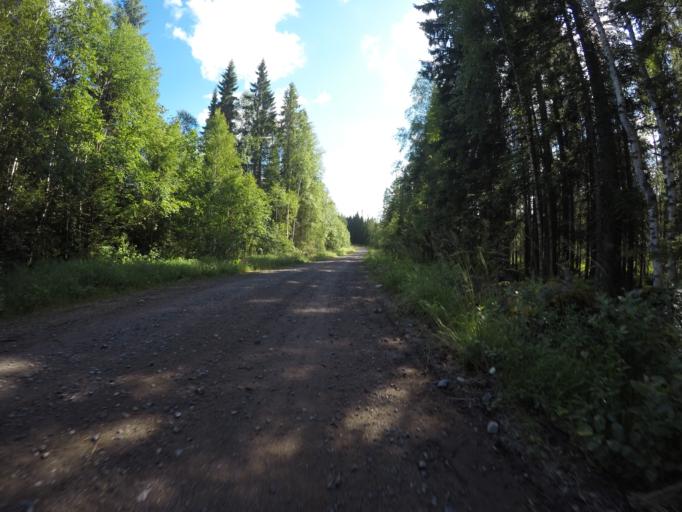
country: SE
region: Dalarna
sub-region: Ludvika Kommun
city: Abborrberget
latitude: 60.0084
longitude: 14.6099
